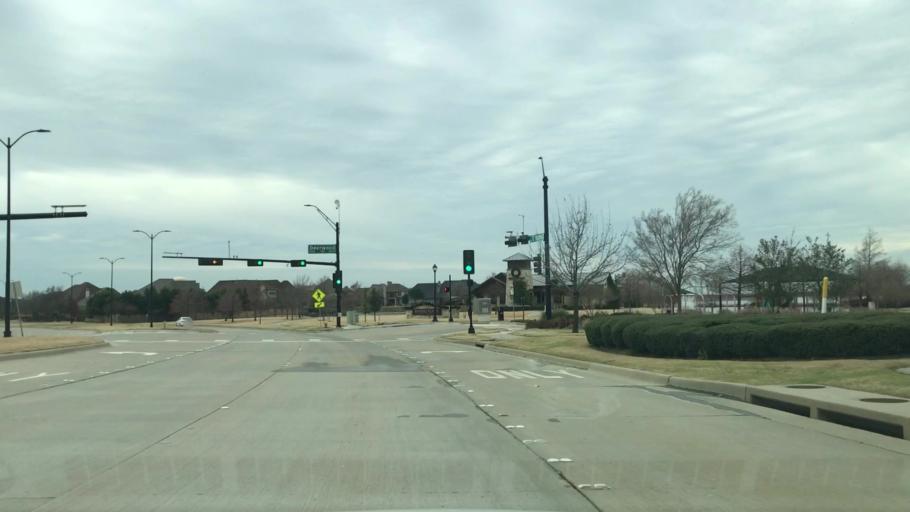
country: US
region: Texas
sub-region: Denton County
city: The Colony
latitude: 33.1273
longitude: -96.8940
